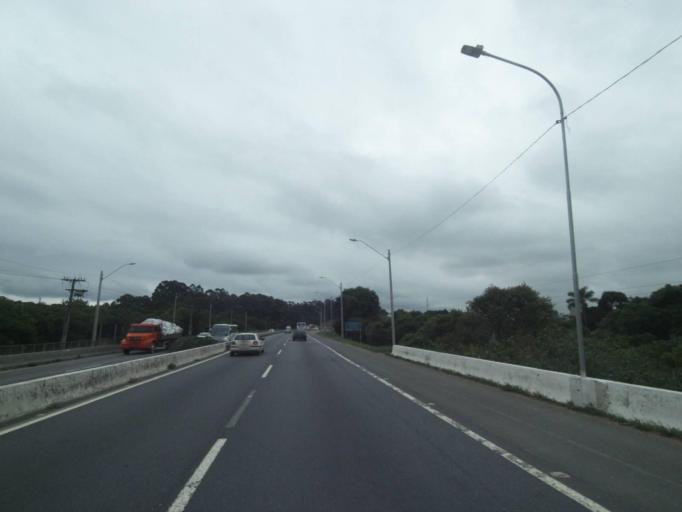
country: BR
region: Parana
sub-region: Araucaria
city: Araucaria
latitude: -25.5557
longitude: -49.3424
